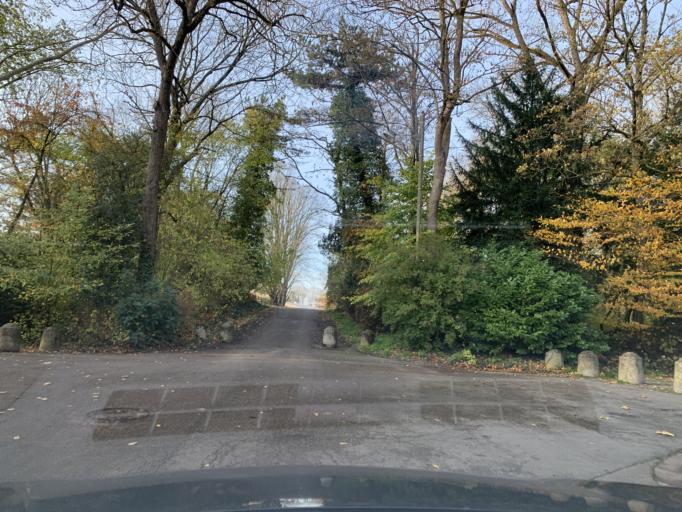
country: FR
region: Nord-Pas-de-Calais
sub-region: Departement du Nord
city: Cambrai
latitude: 50.1686
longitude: 3.2421
